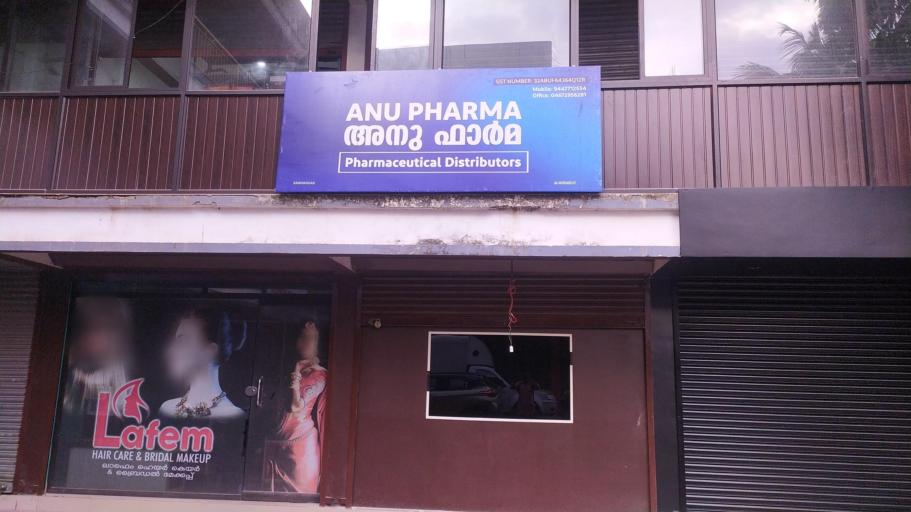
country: IN
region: Kerala
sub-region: Kasaragod District
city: Kannangad
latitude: 12.3229
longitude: 75.0896
